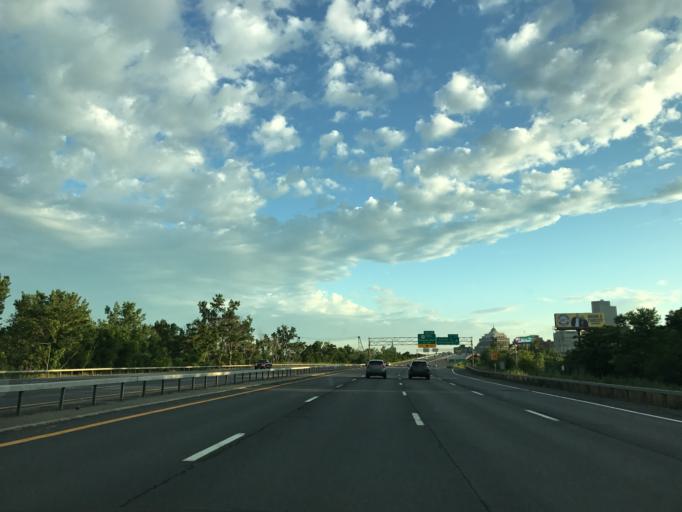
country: US
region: New York
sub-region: Rensselaer County
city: Rensselaer
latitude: 42.6611
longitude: -73.7378
